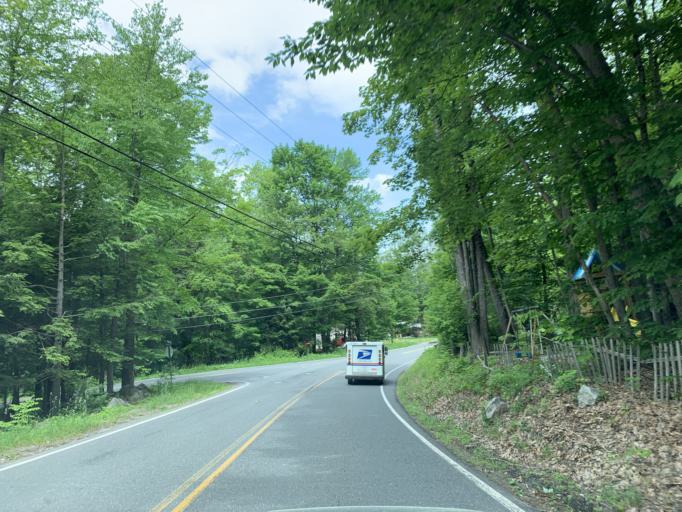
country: US
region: Massachusetts
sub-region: Hampshire County
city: Westhampton
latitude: 42.2387
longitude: -72.8552
